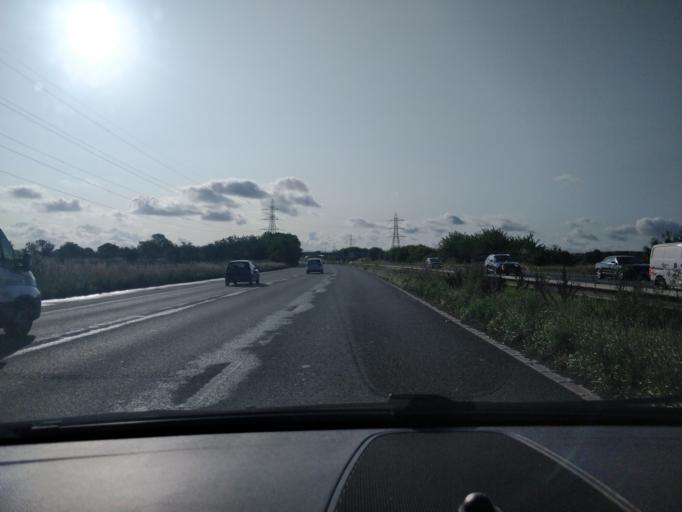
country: GB
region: England
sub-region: Sefton
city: Melling
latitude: 53.4863
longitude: -2.9329
